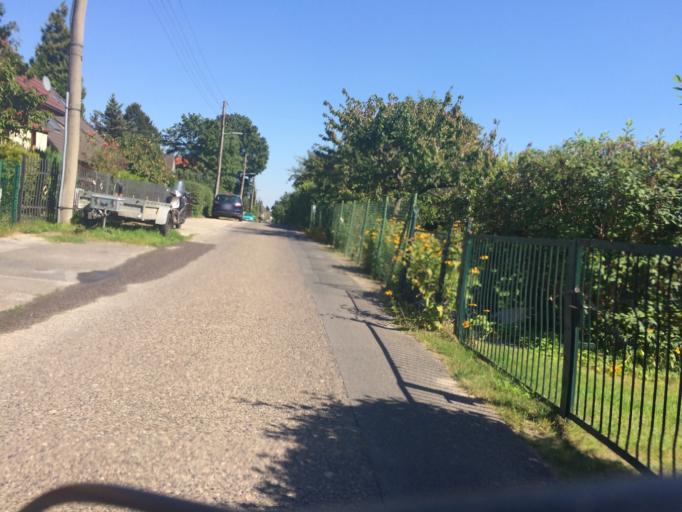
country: DE
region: Berlin
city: Niederschonhausen
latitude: 52.5931
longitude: 13.4060
